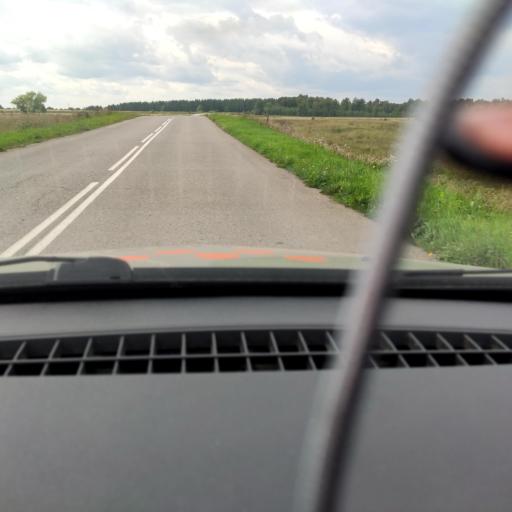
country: RU
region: Bashkortostan
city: Iglino
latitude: 54.7804
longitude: 56.5449
